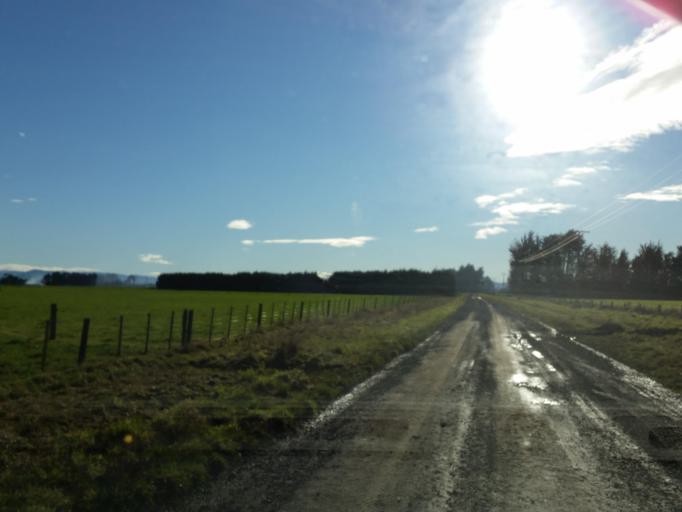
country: NZ
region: Southland
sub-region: Southland District
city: Riverton
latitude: -46.1392
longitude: 168.1029
